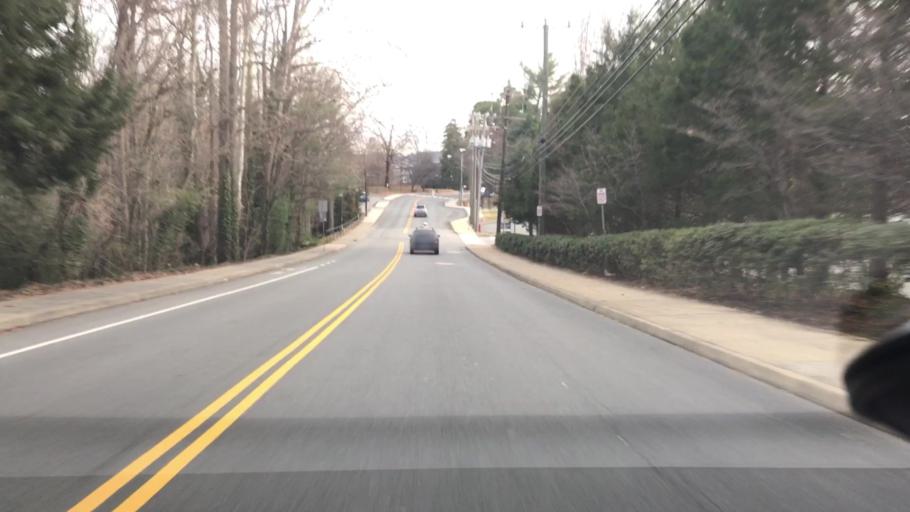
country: US
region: Virginia
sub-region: City of Charlottesville
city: Charlottesville
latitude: 38.0375
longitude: -78.5148
